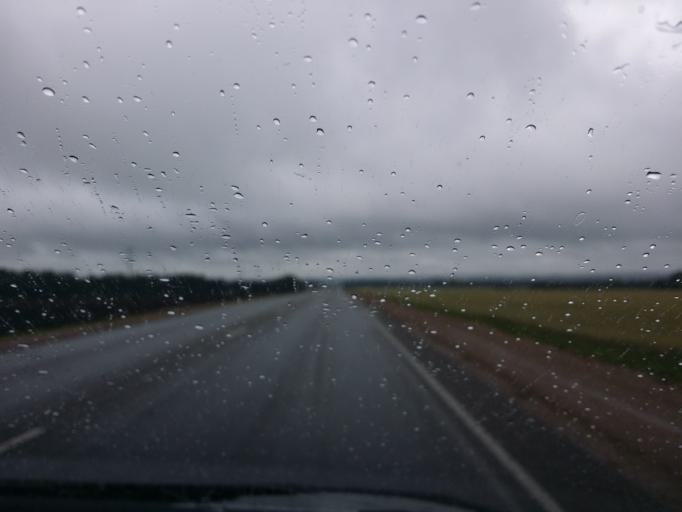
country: RU
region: Altai Krai
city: Nalobikha
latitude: 53.2412
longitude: 84.5930
